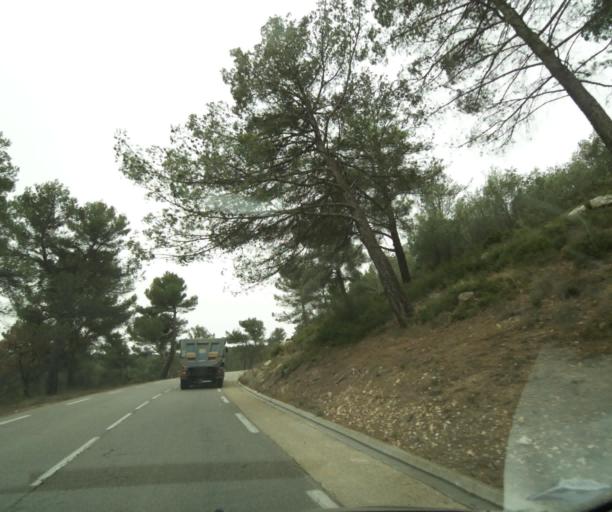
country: FR
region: Provence-Alpes-Cote d'Azur
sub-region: Departement des Bouches-du-Rhone
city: Belcodene
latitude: 43.4262
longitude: 5.6197
